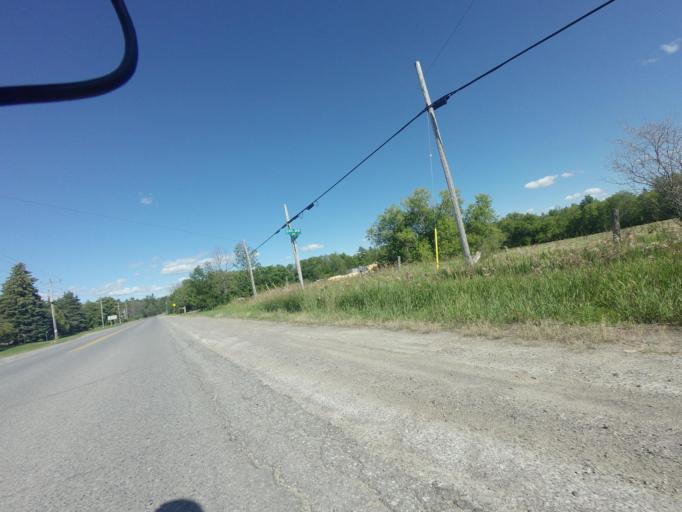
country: CA
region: Ontario
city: Arnprior
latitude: 45.4164
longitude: -76.4290
